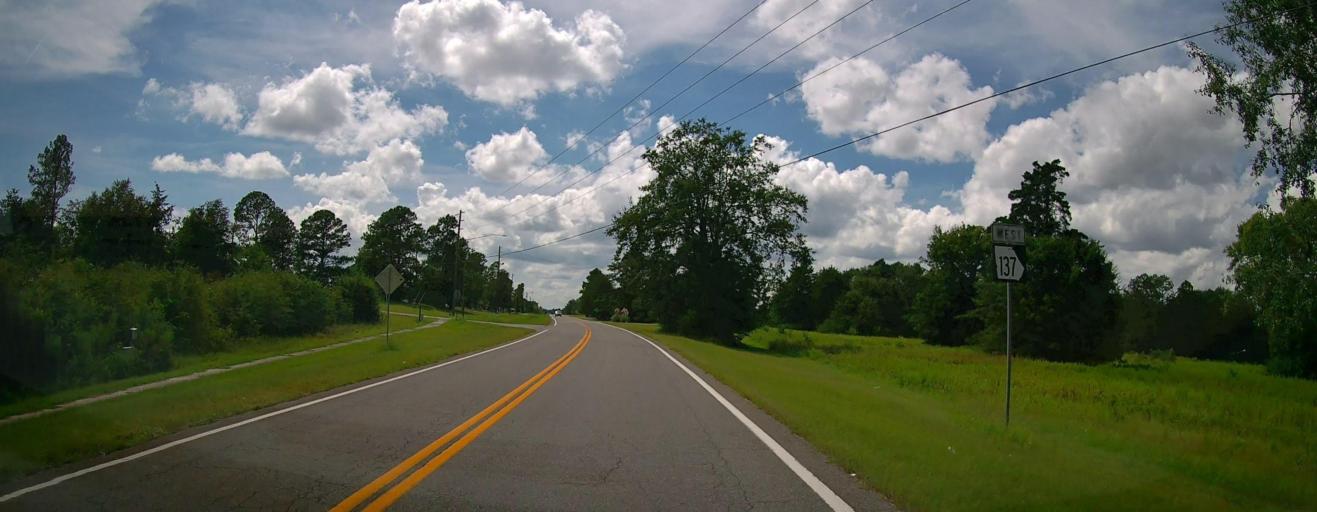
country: US
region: Georgia
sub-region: Taylor County
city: Butler
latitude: 32.5586
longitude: -84.2460
